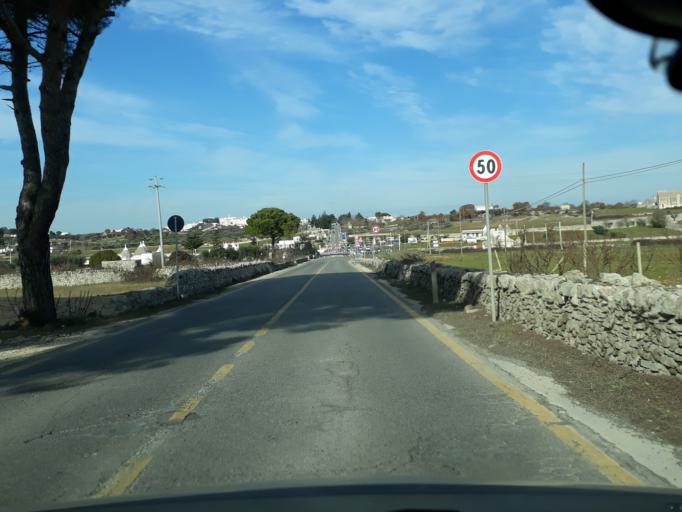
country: IT
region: Apulia
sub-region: Provincia di Bari
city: Locorotondo
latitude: 40.7338
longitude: 17.3326
